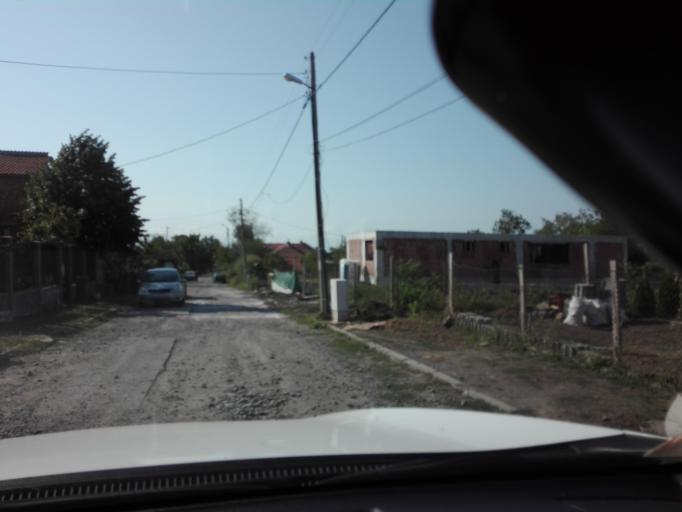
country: BG
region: Burgas
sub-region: Obshtina Kameno
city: Kameno
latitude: 42.6276
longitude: 27.3871
